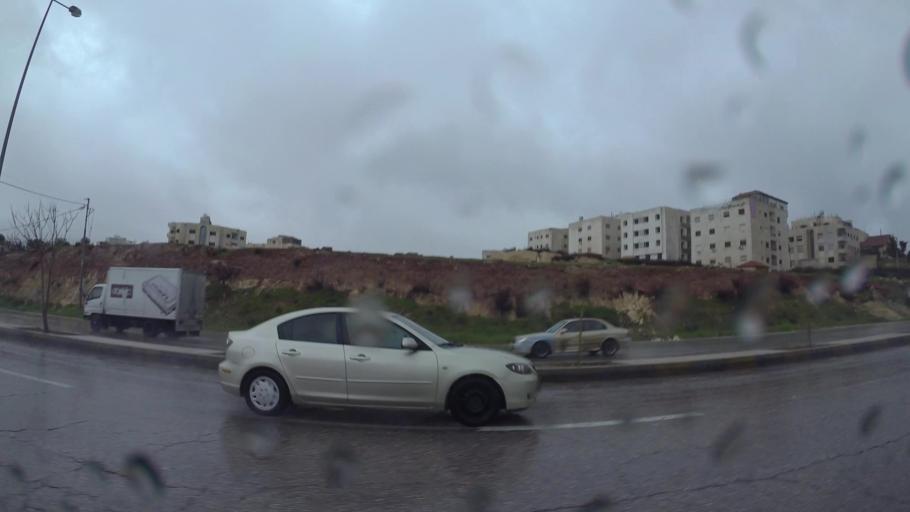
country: JO
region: Amman
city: Al Jubayhah
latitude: 32.0380
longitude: 35.8907
